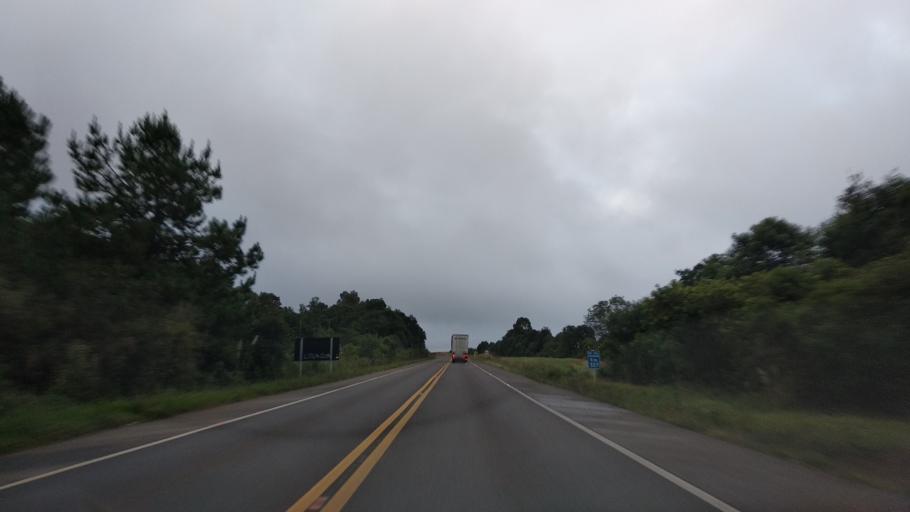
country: BR
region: Santa Catarina
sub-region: Campos Novos
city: Campos Novos
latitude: -27.3850
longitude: -51.1077
